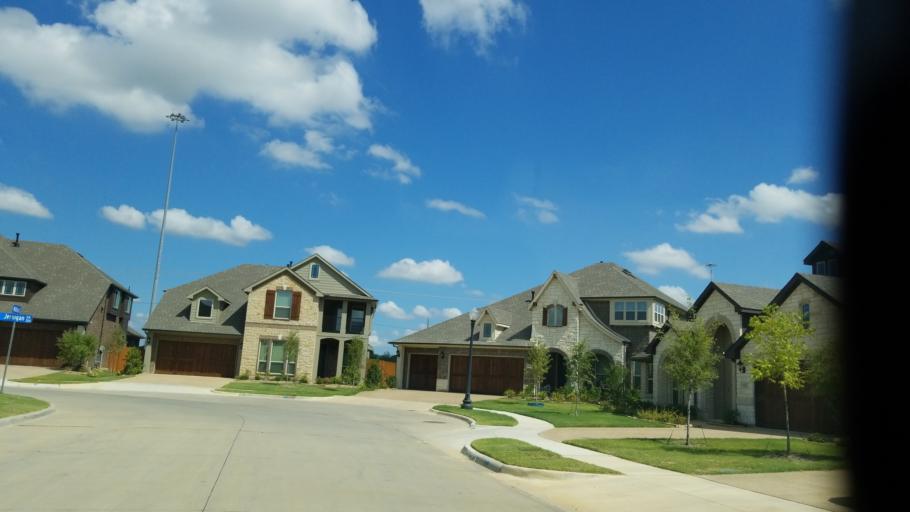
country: US
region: Texas
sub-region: Tarrant County
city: Euless
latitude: 32.8363
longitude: -97.0772
